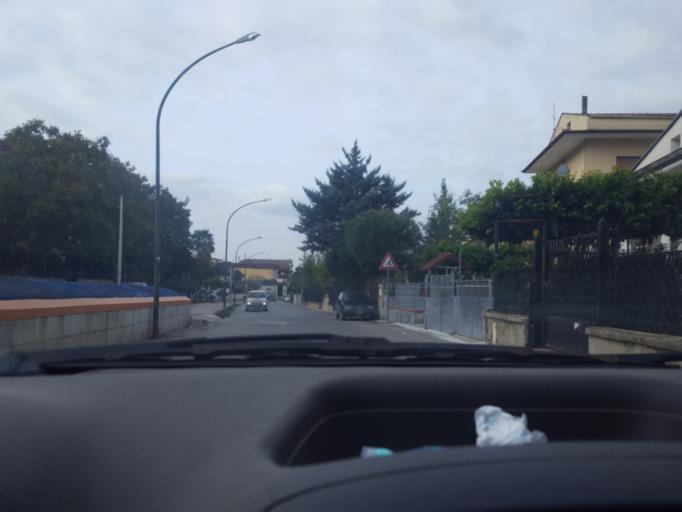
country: IT
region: Campania
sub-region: Provincia di Caserta
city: Arienzo
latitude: 41.0267
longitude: 14.4998
